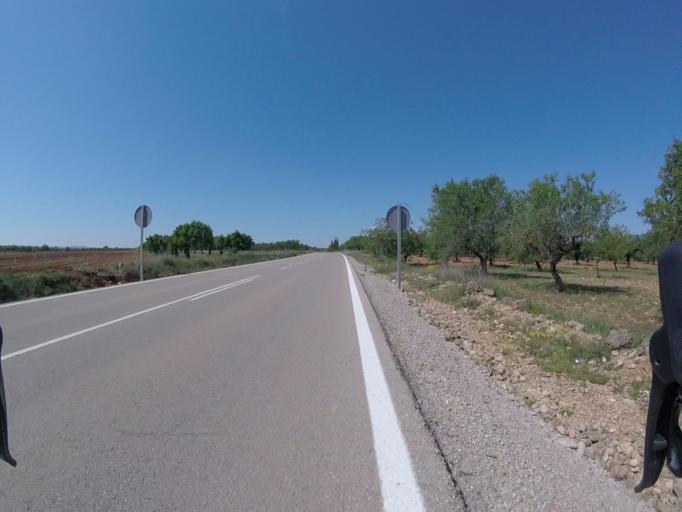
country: ES
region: Valencia
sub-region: Provincia de Castello
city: Benlloch
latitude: 40.2085
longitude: 0.0174
